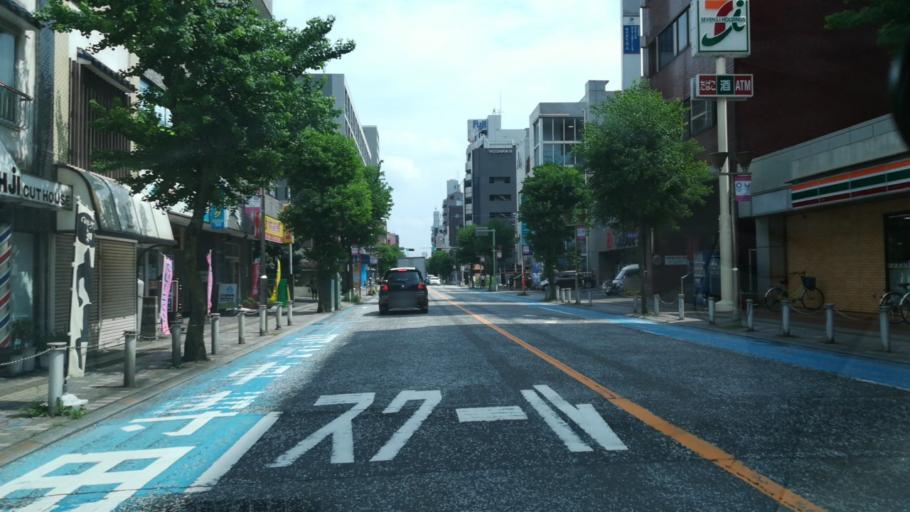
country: JP
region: Tokyo
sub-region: Machida-shi
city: Machida
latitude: 35.5779
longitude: 139.3750
